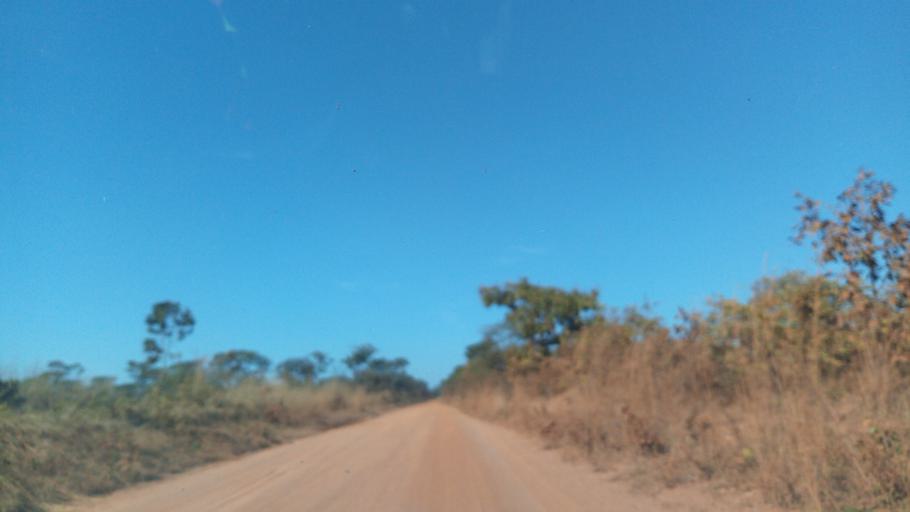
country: ZM
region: Luapula
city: Mwense
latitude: -10.6494
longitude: 28.4091
